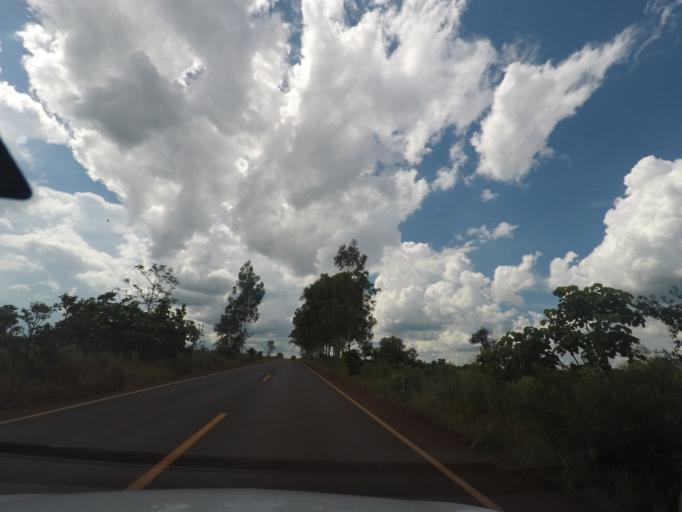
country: BR
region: Minas Gerais
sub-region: Conceicao Das Alagoas
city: Conceicao das Alagoas
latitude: -19.7976
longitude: -48.5823
